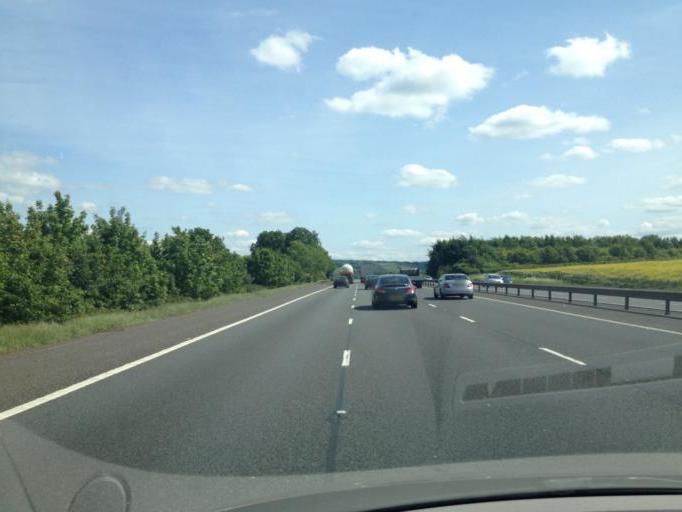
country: GB
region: England
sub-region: Oxfordshire
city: Watlington
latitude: 51.6897
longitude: -0.9792
